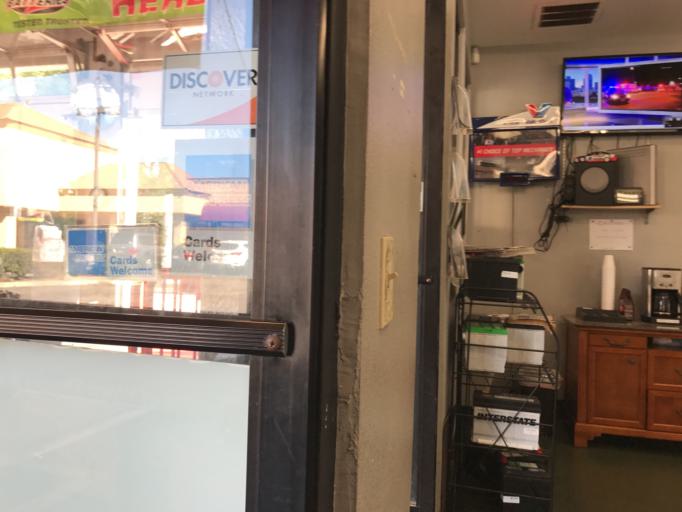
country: US
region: California
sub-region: Orange County
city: Cypress
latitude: 33.8174
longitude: -118.0290
